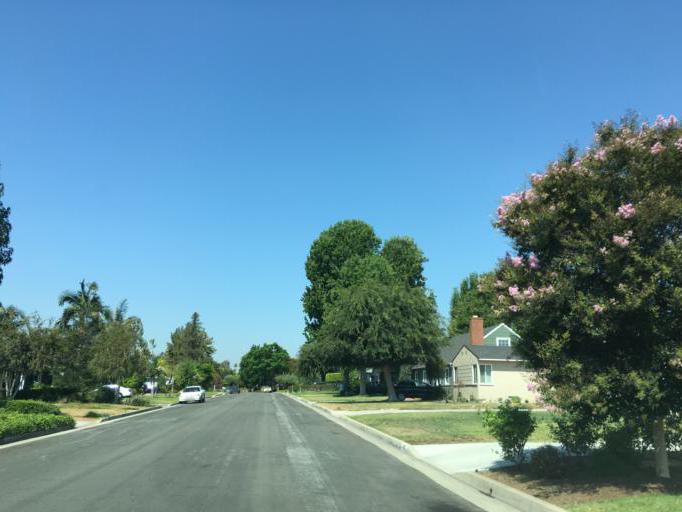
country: US
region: California
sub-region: Los Angeles County
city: San Marino
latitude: 34.1194
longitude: -118.0856
